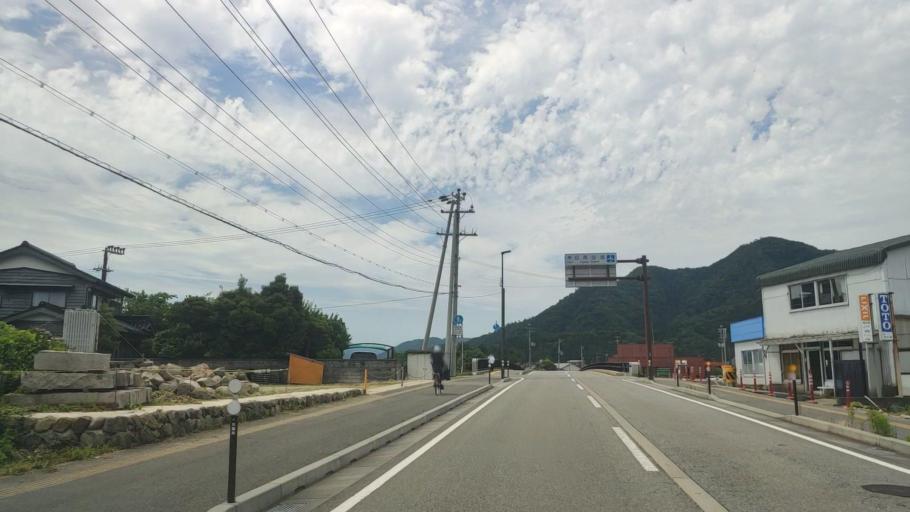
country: JP
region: Hyogo
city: Toyooka
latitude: 35.6548
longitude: 134.7609
